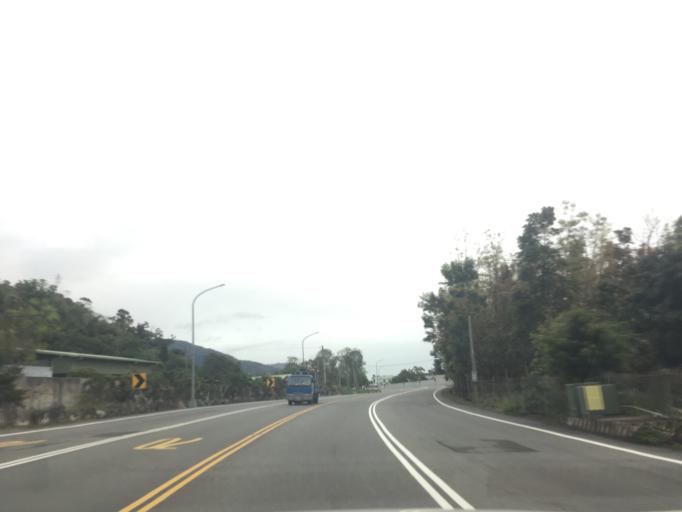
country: TW
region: Taiwan
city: Taitung City
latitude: 22.7394
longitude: 121.0566
